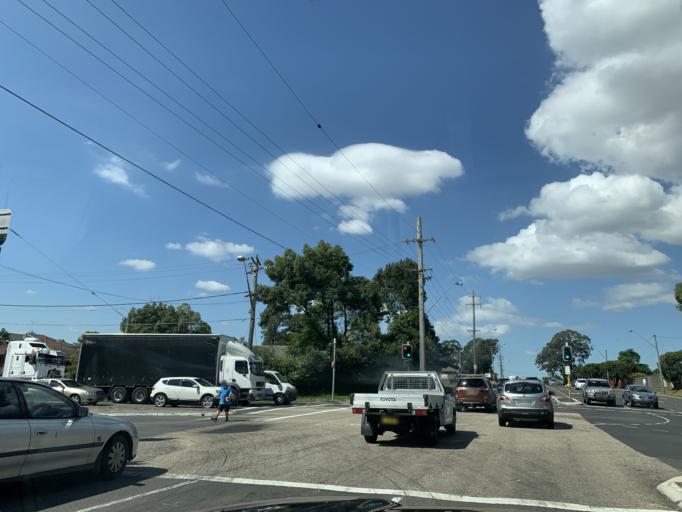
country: AU
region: New South Wales
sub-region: Blacktown
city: Mount Druitt
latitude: -33.7714
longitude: 150.7792
